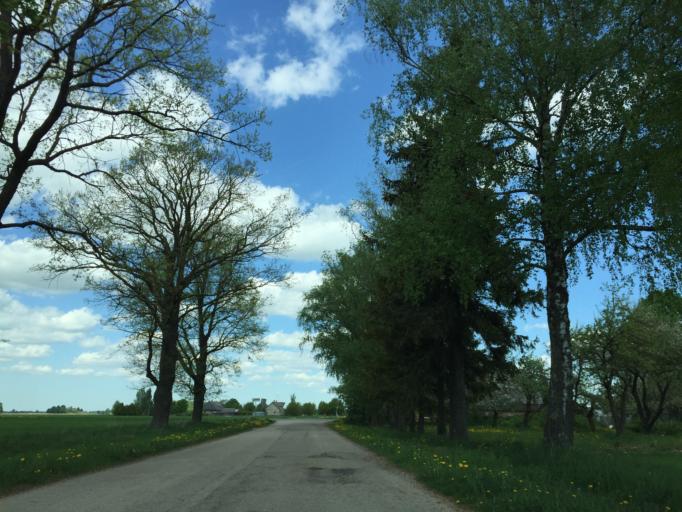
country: LV
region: Rundales
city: Pilsrundale
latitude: 56.4311
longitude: 24.0794
